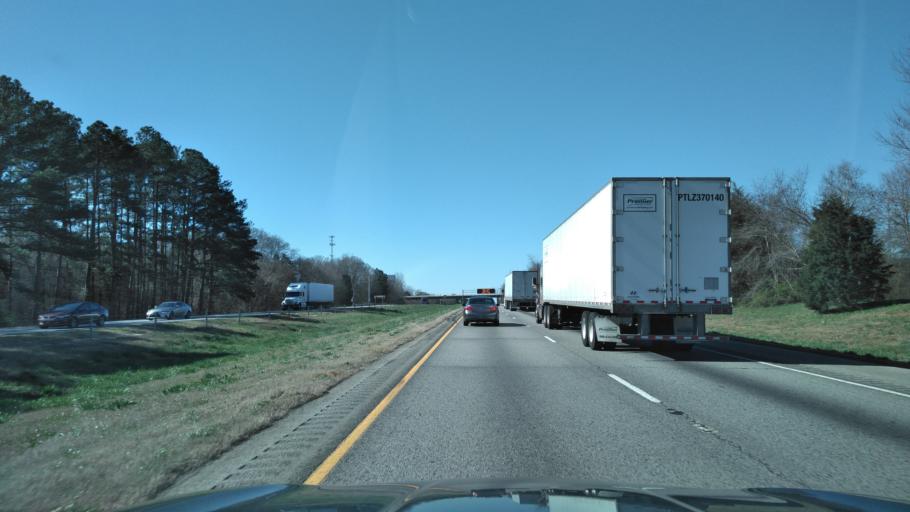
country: US
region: Georgia
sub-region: Franklin County
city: Lavonia
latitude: 34.4231
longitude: -83.1630
